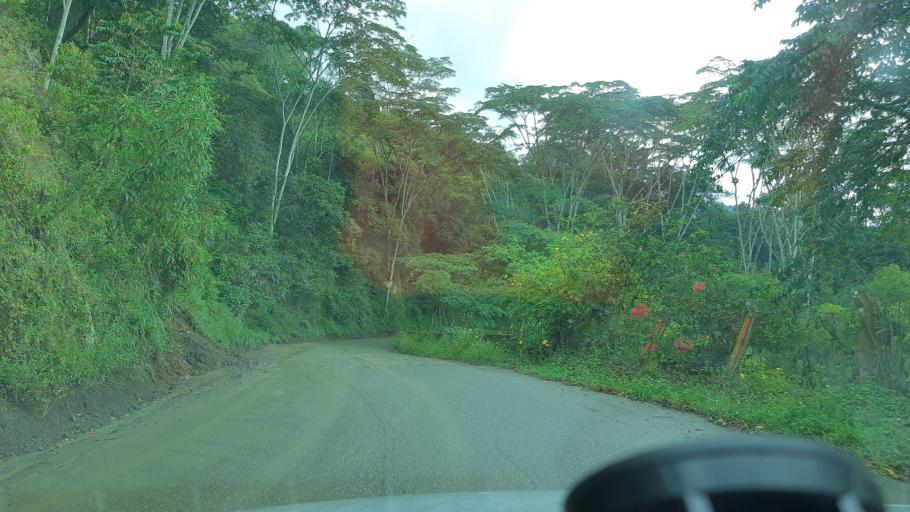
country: CO
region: Boyaca
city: Chinavita
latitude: 5.1261
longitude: -73.3626
